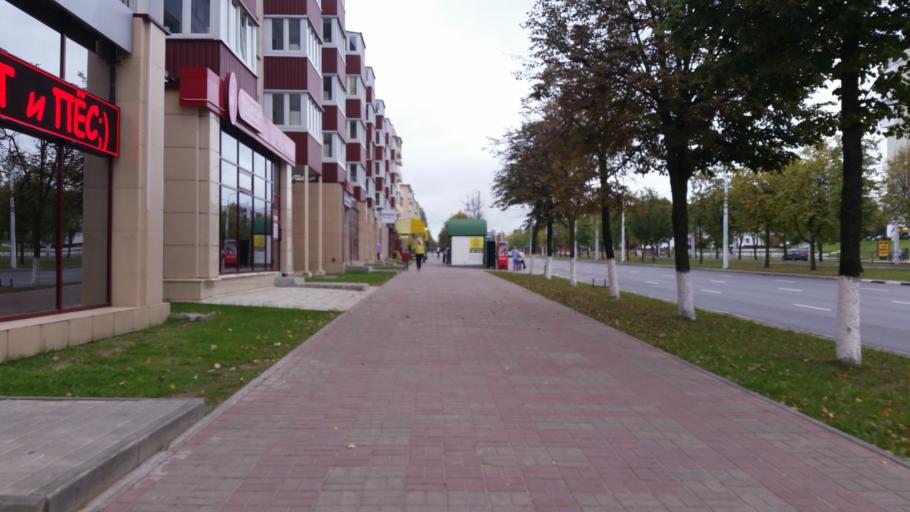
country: BY
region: Vitebsk
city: Vitebsk
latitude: 55.1811
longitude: 30.2135
